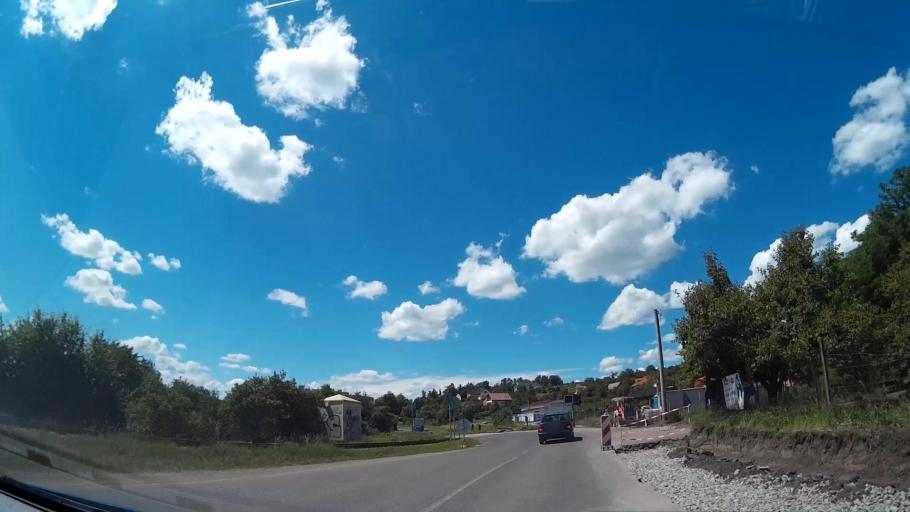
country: CZ
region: South Moravian
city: Ivancice
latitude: 49.1061
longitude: 16.3631
